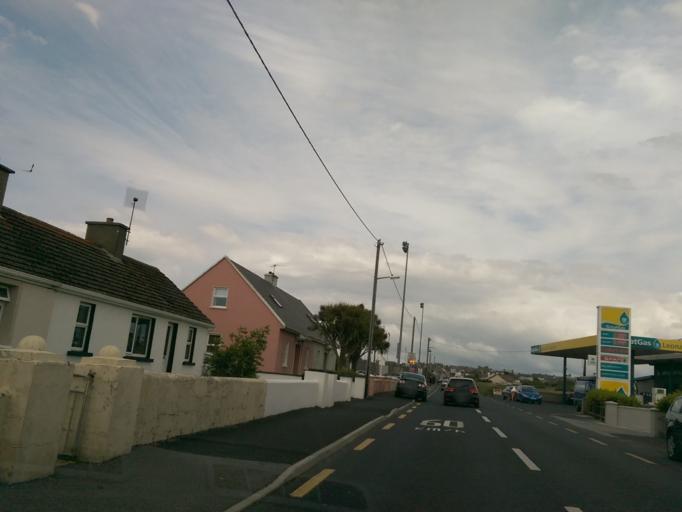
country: IE
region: Munster
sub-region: An Clar
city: Kilrush
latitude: 52.8511
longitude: -9.4097
